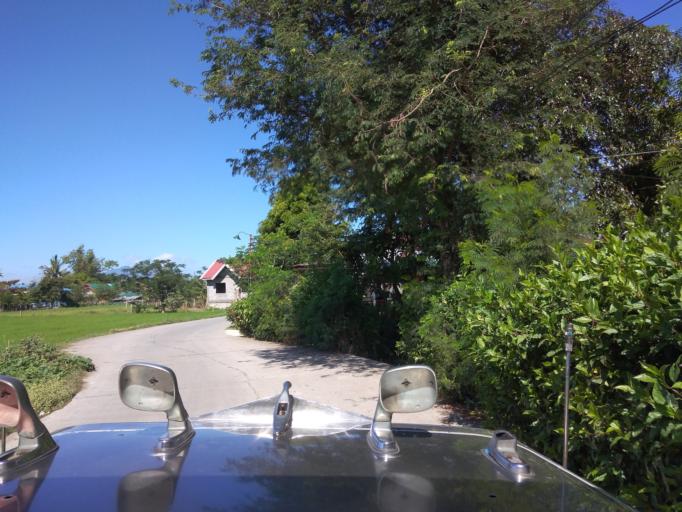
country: PH
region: Central Luzon
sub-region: Province of Pampanga
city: Batasan Bata
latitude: 15.1647
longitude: 120.9190
